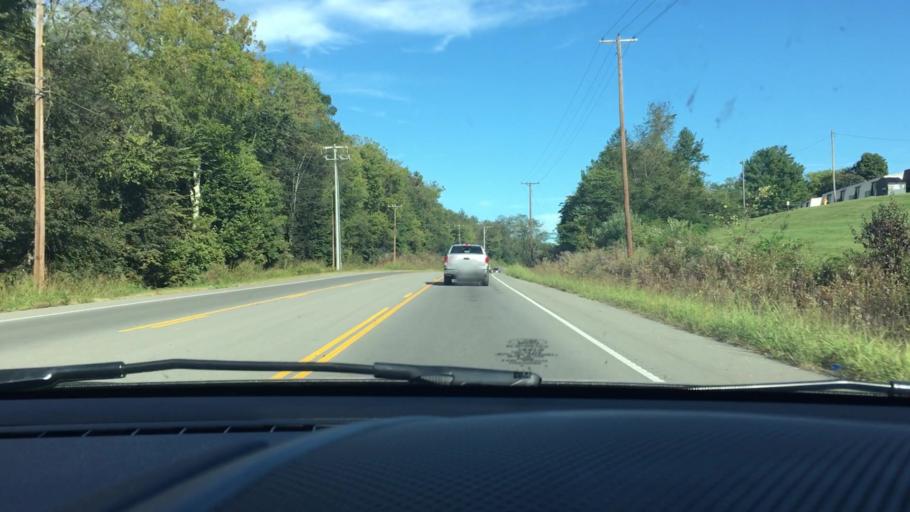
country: US
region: Tennessee
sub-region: Montgomery County
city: Clarksville
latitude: 36.5014
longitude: -87.3026
